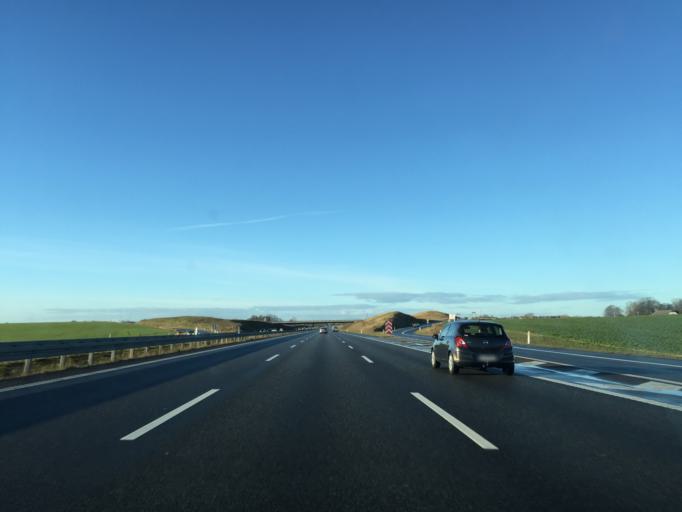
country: DK
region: South Denmark
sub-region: Middelfart Kommune
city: Norre Aby
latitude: 55.4922
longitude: 9.8218
